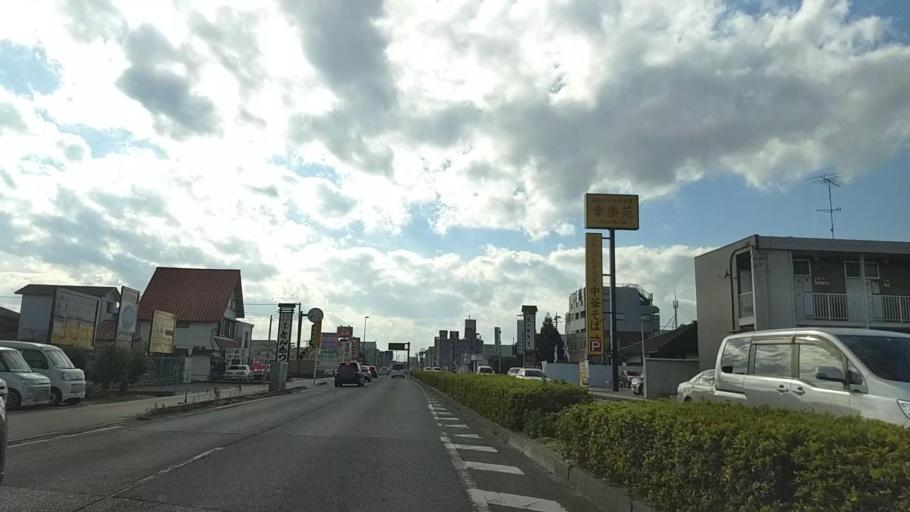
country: JP
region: Chiba
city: Togane
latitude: 35.5565
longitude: 140.3683
